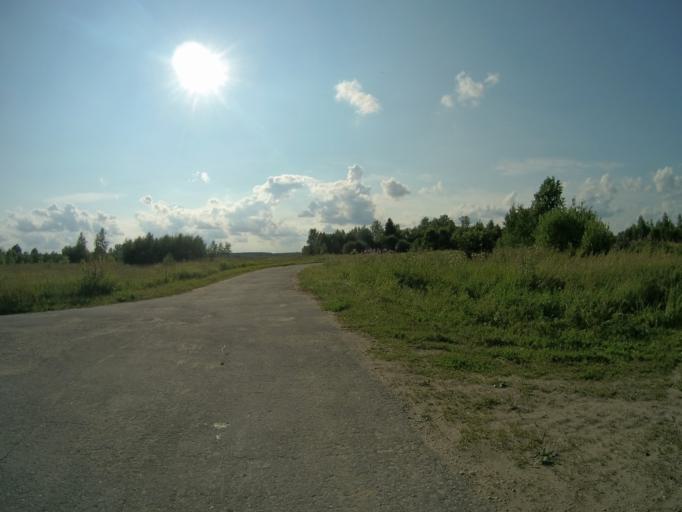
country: RU
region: Vladimir
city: Orgtrud
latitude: 56.3449
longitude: 40.6925
